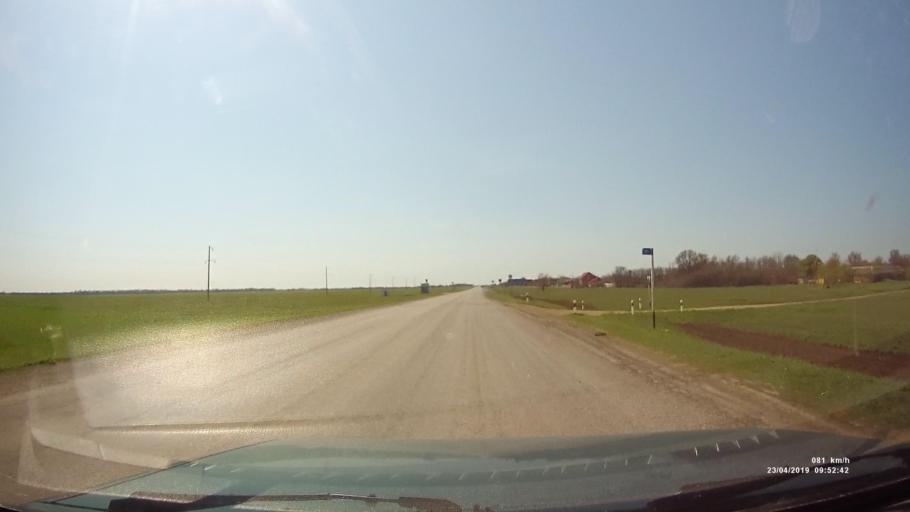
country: RU
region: Rostov
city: Orlovskiy
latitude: 46.8416
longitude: 42.0471
